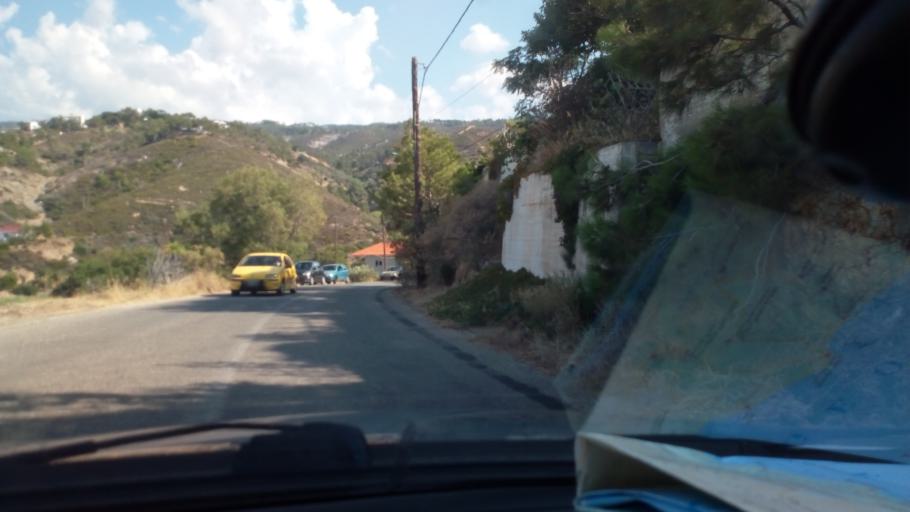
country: GR
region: North Aegean
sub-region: Nomos Samou
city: Agios Kirykos
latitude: 37.6306
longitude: 26.0888
